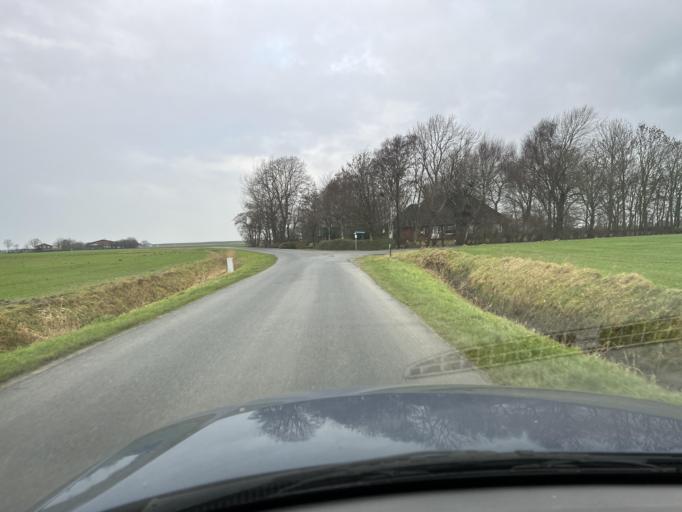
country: DE
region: Schleswig-Holstein
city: Hillgroven
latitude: 54.2190
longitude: 8.8742
